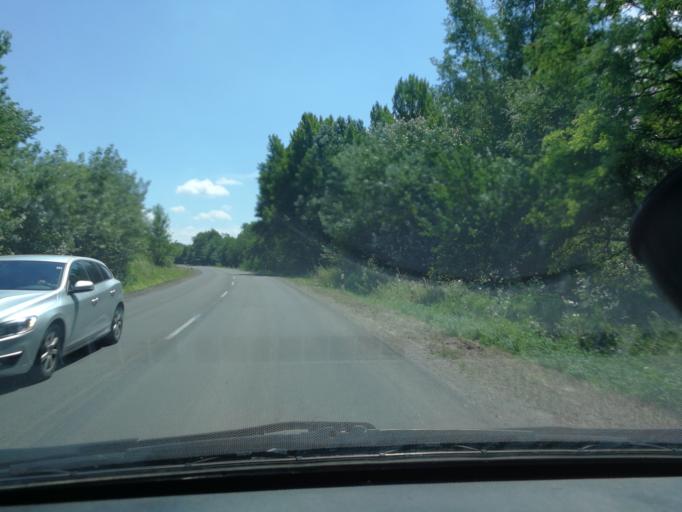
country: HU
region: Pest
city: Domsod
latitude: 47.1295
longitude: 18.9963
